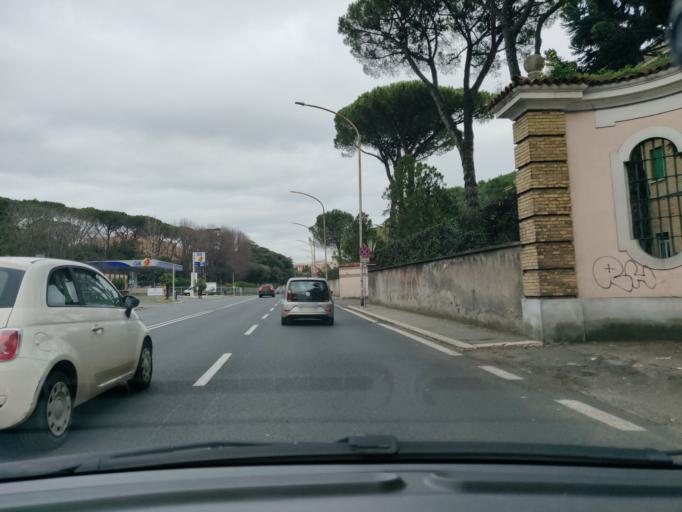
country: VA
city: Vatican City
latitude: 41.8970
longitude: 12.4212
